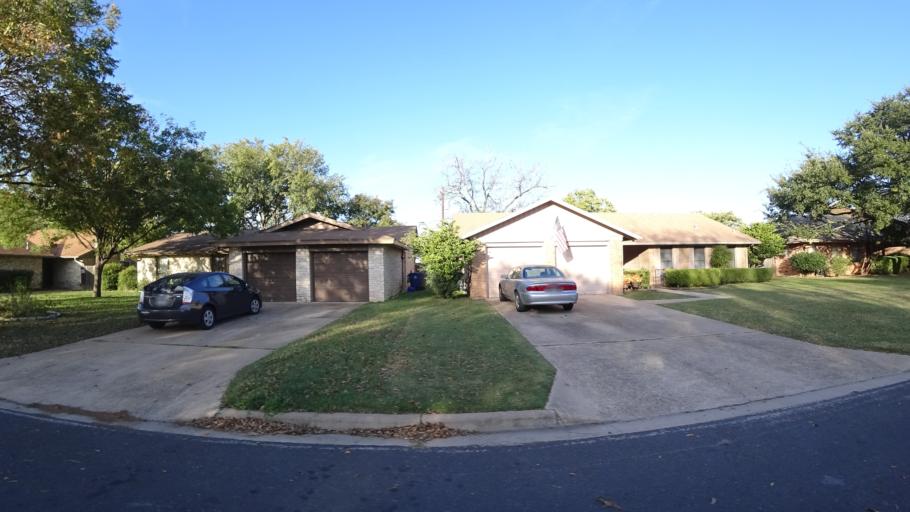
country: US
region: Texas
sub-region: Williamson County
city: Jollyville
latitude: 30.3726
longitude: -97.7310
